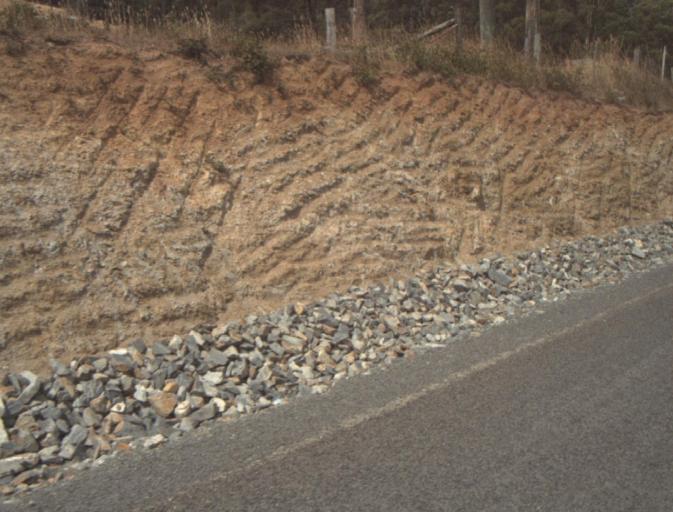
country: AU
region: Tasmania
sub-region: Launceston
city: Mayfield
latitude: -41.2203
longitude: 147.2069
